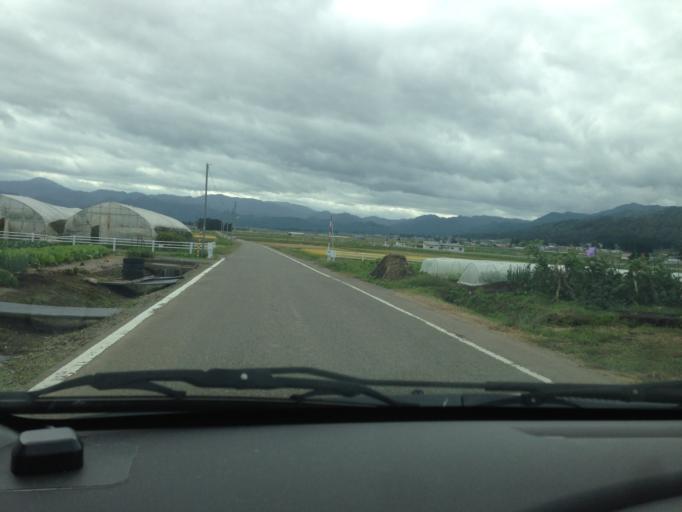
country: JP
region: Fukushima
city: Kitakata
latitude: 37.5057
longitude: 139.8299
